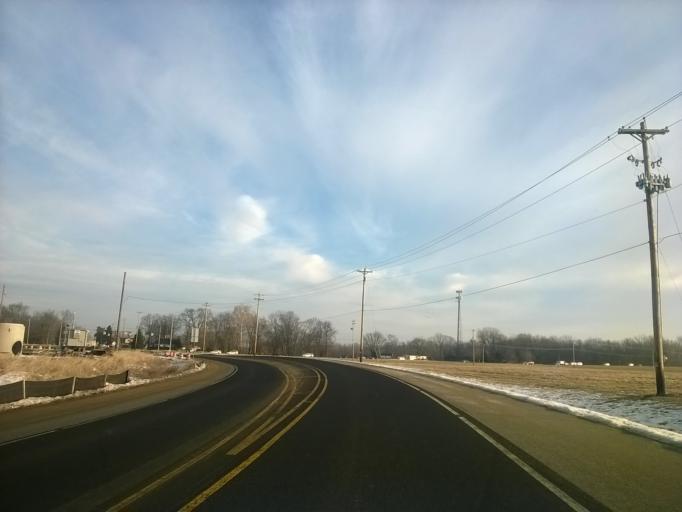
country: US
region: Indiana
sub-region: Hamilton County
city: Fishers
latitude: 39.9979
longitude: -86.0342
